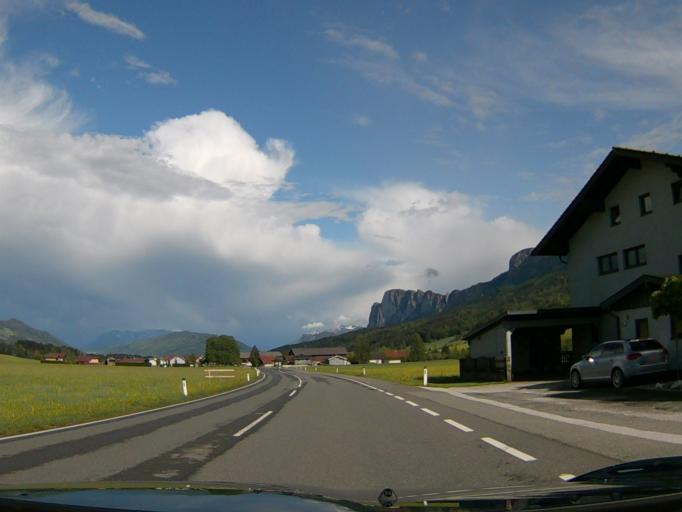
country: AT
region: Salzburg
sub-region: Politischer Bezirk Salzburg-Umgebung
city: Thalgau
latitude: 47.8410
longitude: 13.2708
